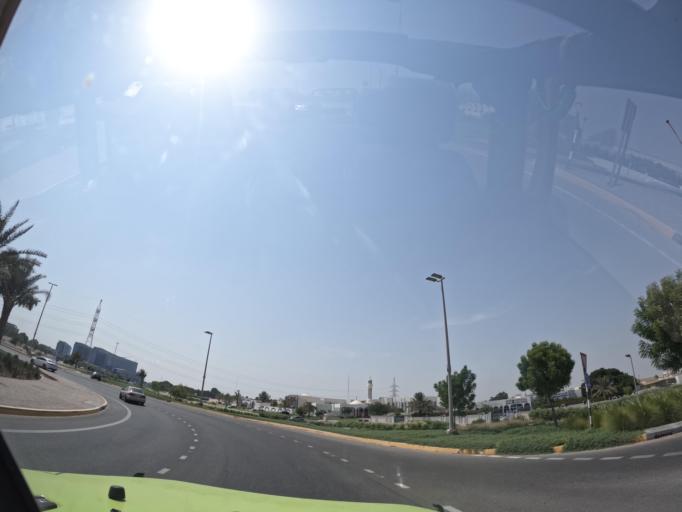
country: AE
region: Abu Dhabi
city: Abu Dhabi
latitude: 24.3300
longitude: 54.6208
